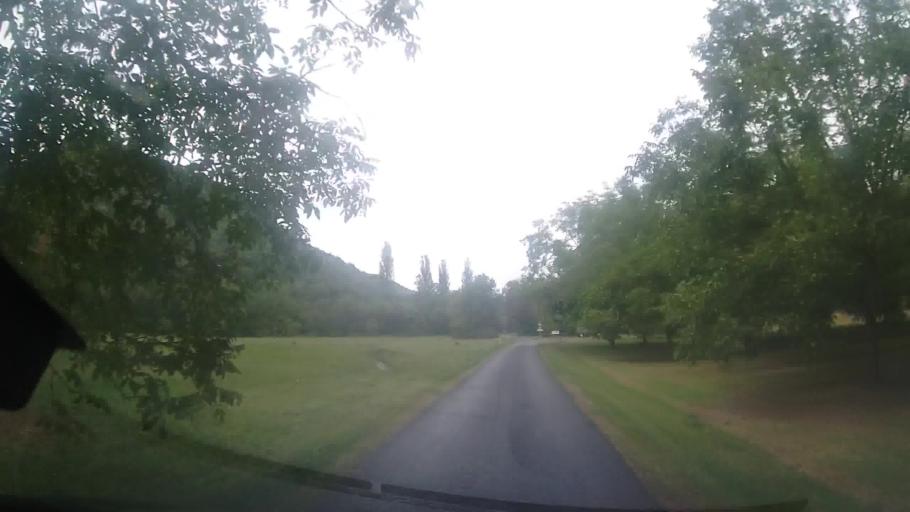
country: FR
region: Aquitaine
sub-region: Departement de la Dordogne
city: Cenac-et-Saint-Julien
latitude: 44.7974
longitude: 1.1637
